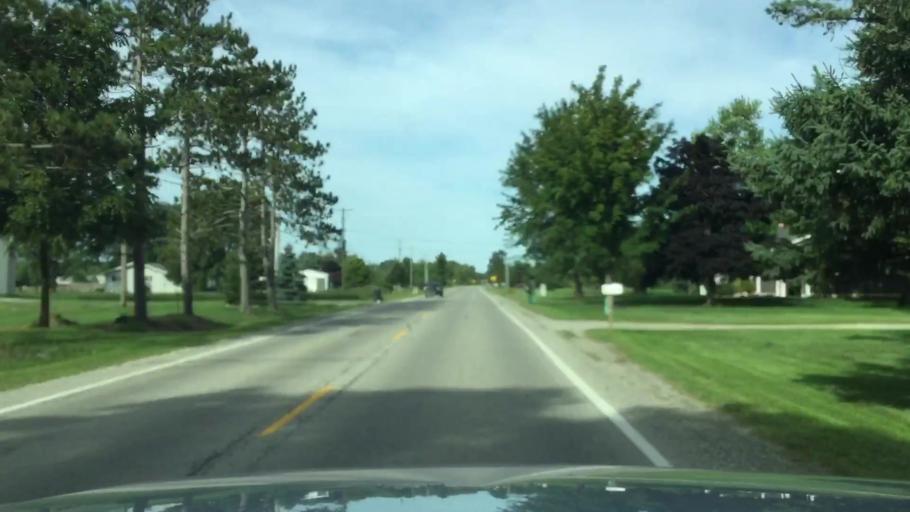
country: US
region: Michigan
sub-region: Genesee County
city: Montrose
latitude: 43.1177
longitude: -83.9233
